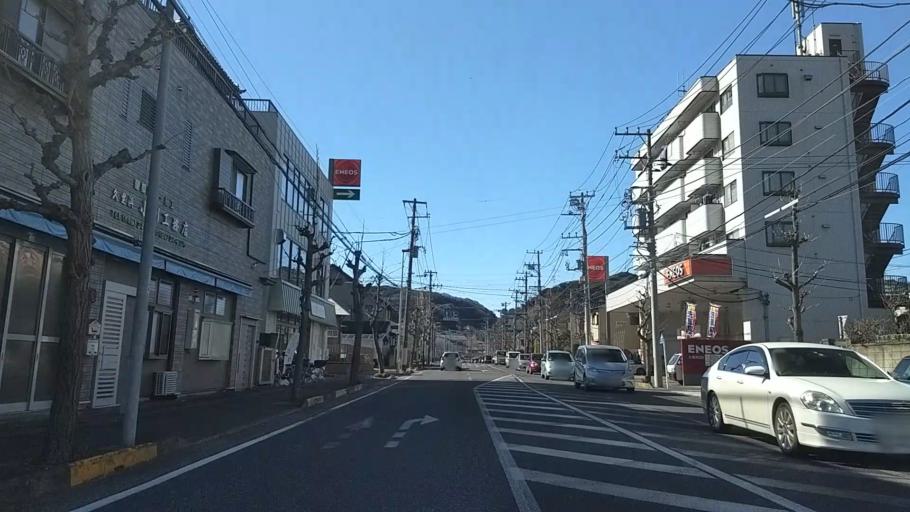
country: JP
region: Kanagawa
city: Yokosuka
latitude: 35.2282
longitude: 139.7023
